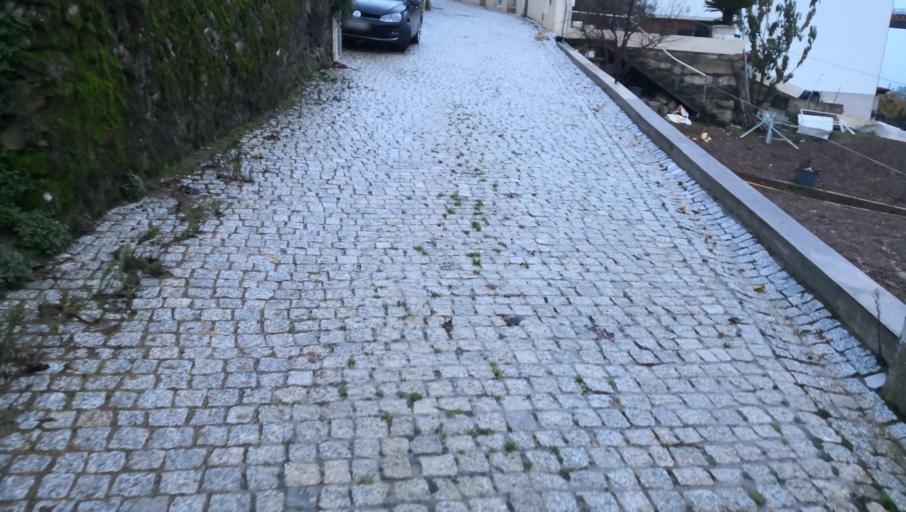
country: PT
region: Vila Real
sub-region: Vila Real
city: Vila Real
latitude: 41.2806
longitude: -7.7465
